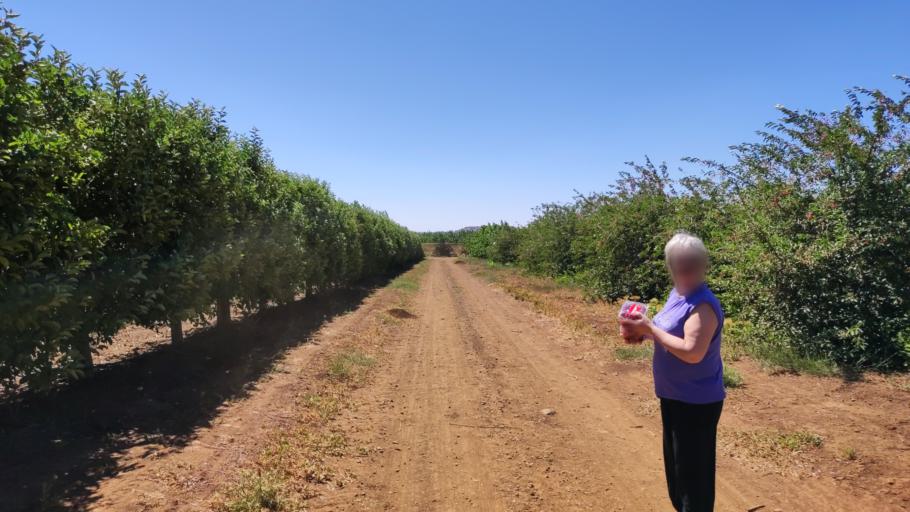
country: SY
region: Quneitra
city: Al Qunaytirah
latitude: 33.1206
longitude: 35.8061
